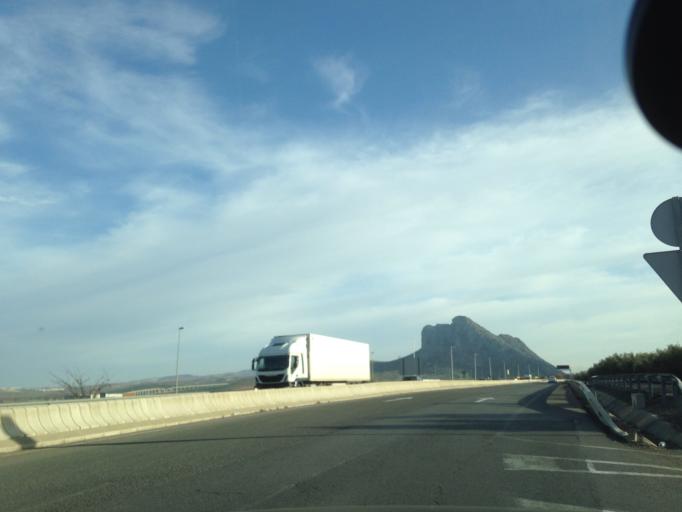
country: ES
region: Andalusia
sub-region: Provincia de Malaga
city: Antequera
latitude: 37.0408
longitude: -4.5171
